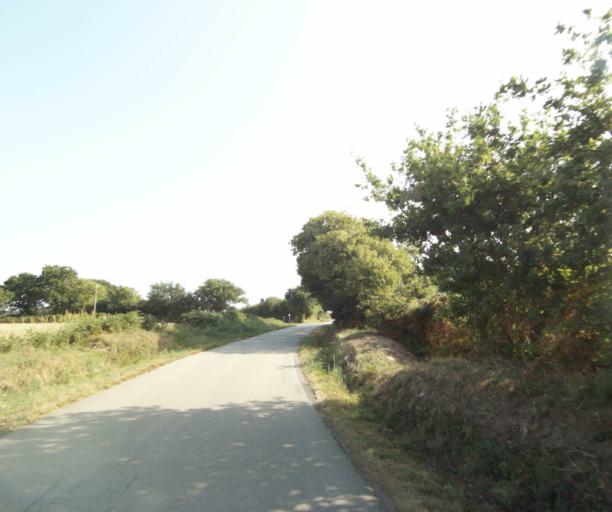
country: FR
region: Brittany
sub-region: Departement du Morbihan
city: Riantec
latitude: 47.7255
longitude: -3.2962
